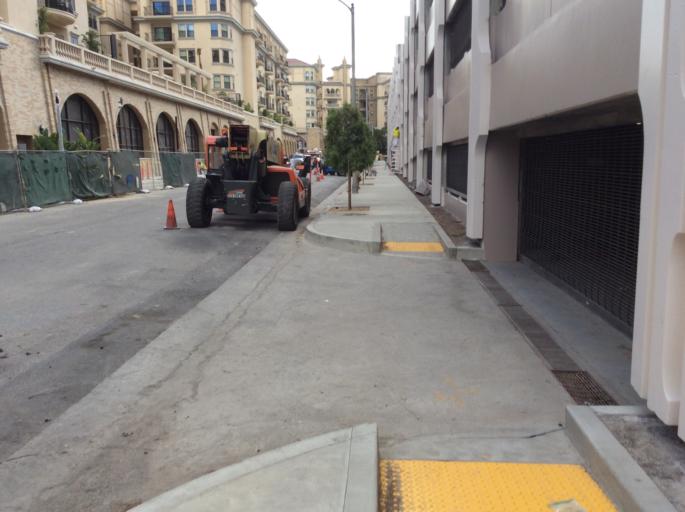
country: US
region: California
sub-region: Los Angeles County
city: Los Angeles
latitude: 34.0600
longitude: -118.2507
